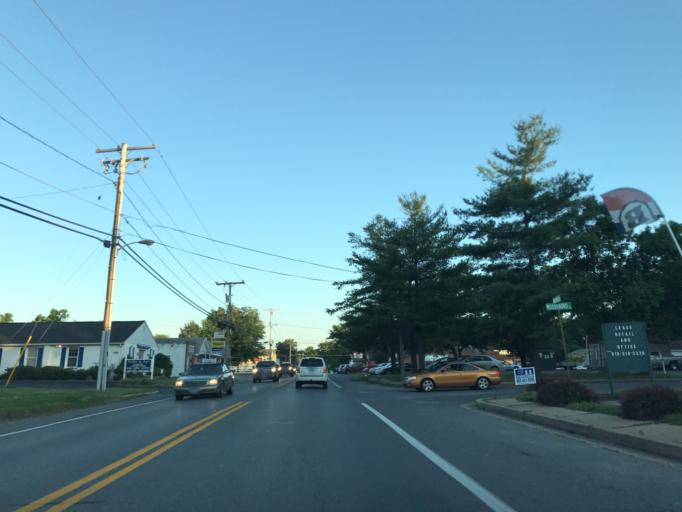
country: US
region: Maryland
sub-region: Anne Arundel County
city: Londontowne
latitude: 38.9338
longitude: -76.5575
